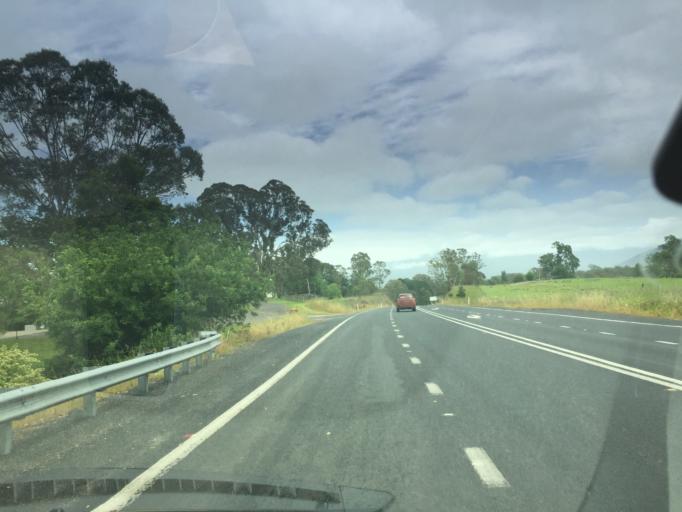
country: AU
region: New South Wales
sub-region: Bega Valley
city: Bega
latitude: -36.6443
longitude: 149.5870
